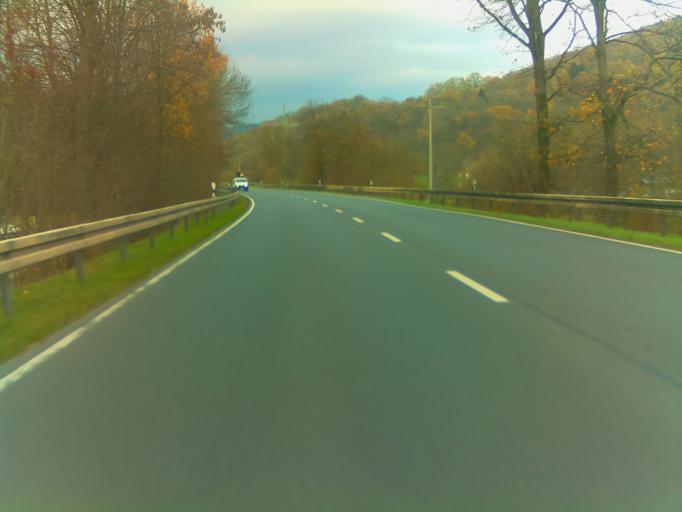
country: DE
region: Bavaria
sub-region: Regierungsbezirk Unterfranken
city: Weilbach
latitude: 49.6892
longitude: 9.2225
